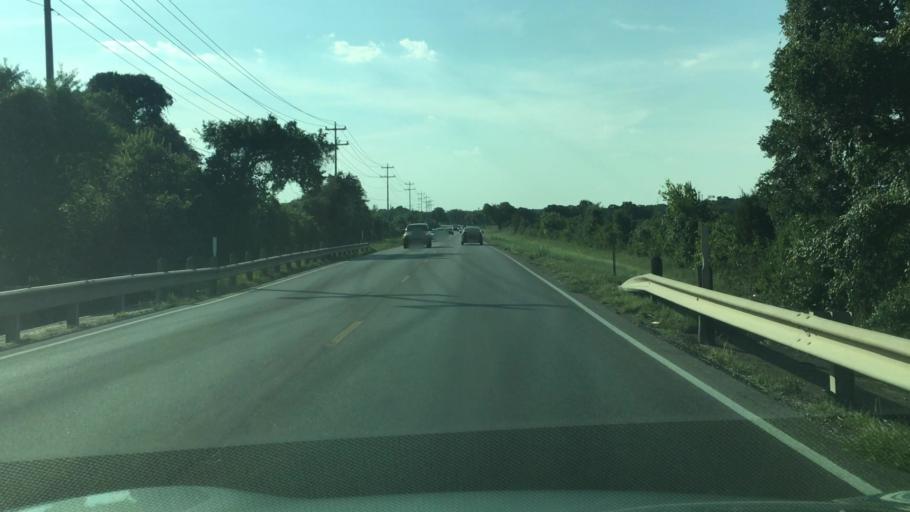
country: US
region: Texas
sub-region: Travis County
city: Shady Hollow
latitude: 30.1107
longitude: -97.9476
